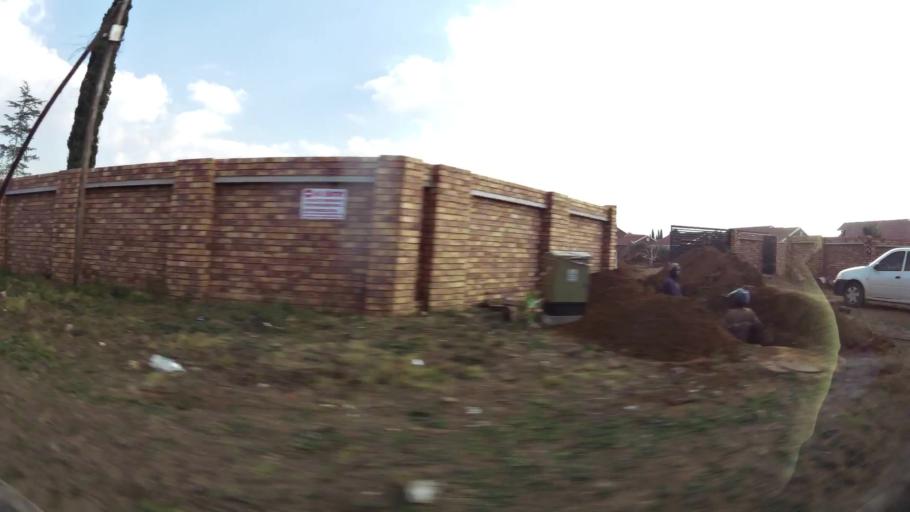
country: ZA
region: Gauteng
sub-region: Ekurhuleni Metropolitan Municipality
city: Benoni
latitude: -26.1115
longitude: 28.2873
